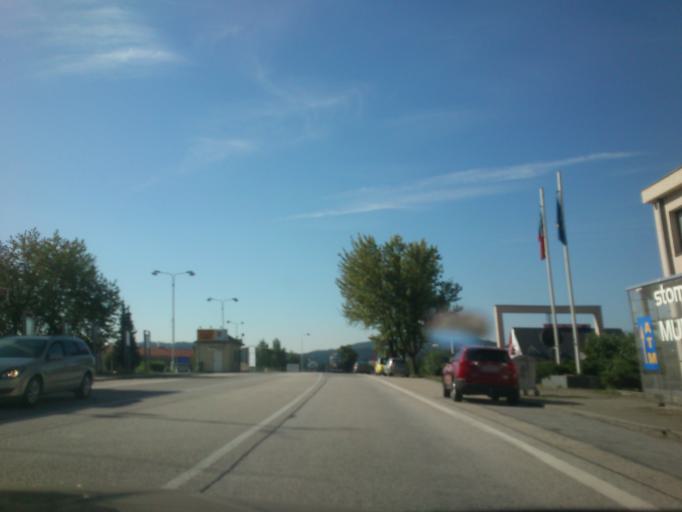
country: CZ
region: Jihocesky
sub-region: Okres Cesky Krumlov
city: Dolni Dvoriste
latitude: 48.6507
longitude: 14.4528
